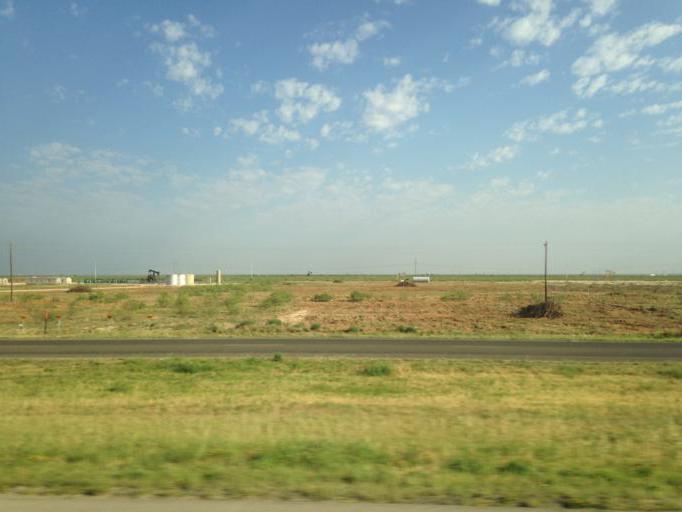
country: US
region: Texas
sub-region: Midland County
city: Midland
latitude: 32.0629
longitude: -101.9445
